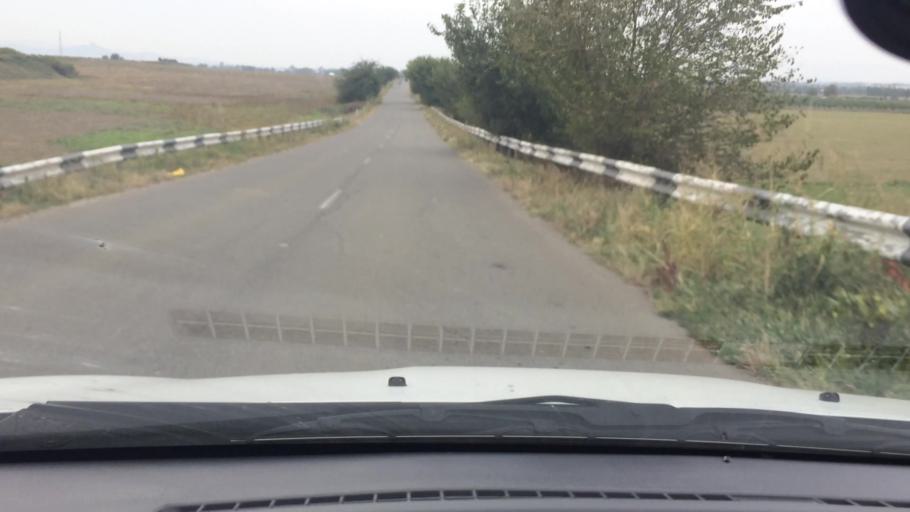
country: AM
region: Tavush
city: Berdavan
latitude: 41.3414
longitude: 44.9930
